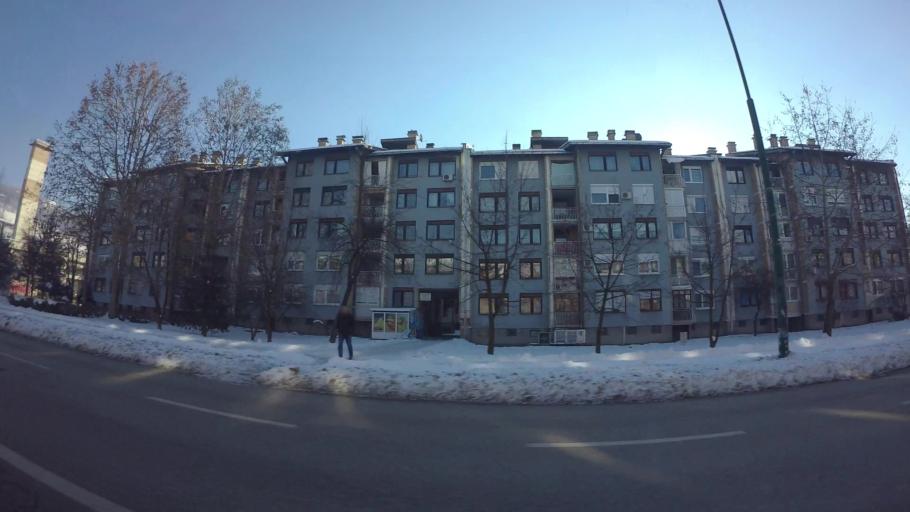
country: BA
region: Federation of Bosnia and Herzegovina
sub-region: Kanton Sarajevo
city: Sarajevo
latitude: 43.8309
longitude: 18.3512
